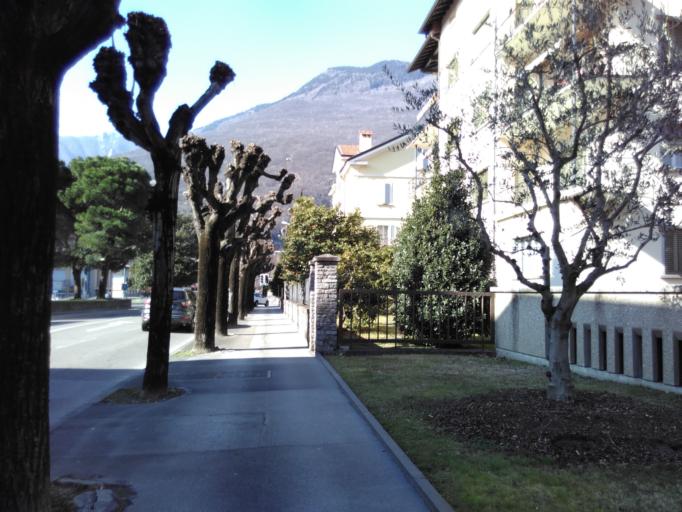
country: CH
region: Ticino
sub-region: Bellinzona District
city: Bellinzona
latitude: 46.1908
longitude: 9.0183
